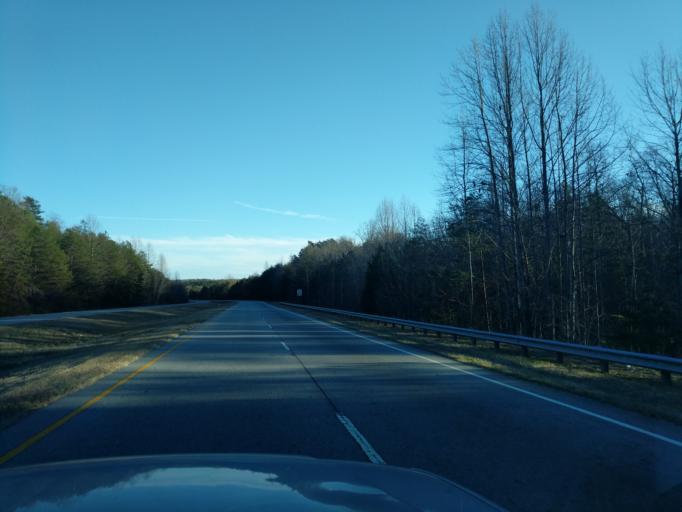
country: US
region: Georgia
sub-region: Stephens County
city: Toccoa
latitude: 34.5688
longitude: -83.4002
